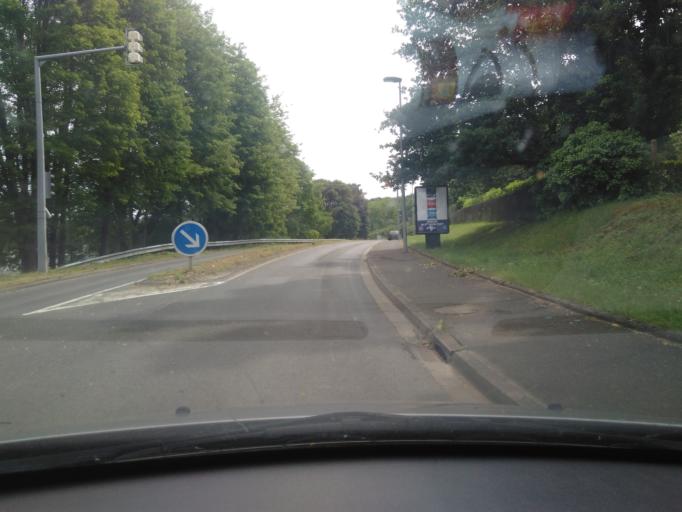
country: FR
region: Centre
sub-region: Departement d'Indre-et-Loire
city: Charge
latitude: 47.4038
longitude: 1.0146
